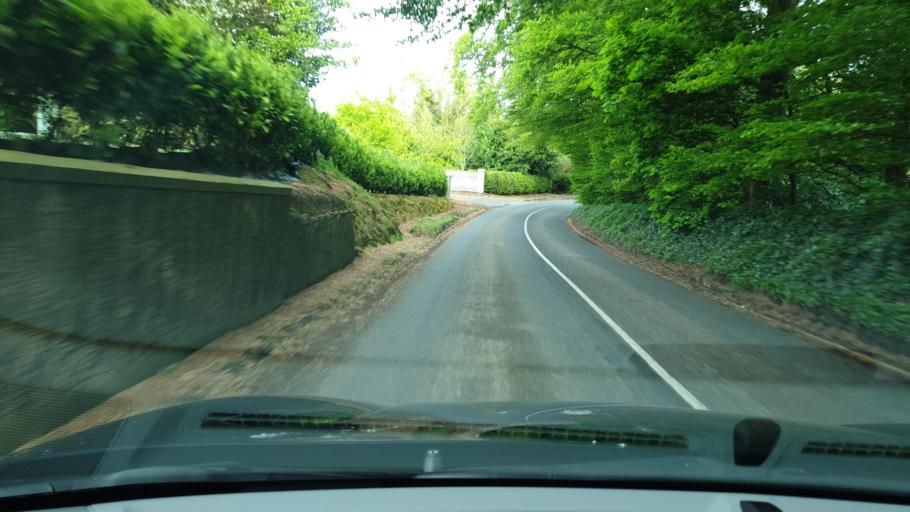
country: IE
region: Leinster
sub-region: An Mhi
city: Ashbourne
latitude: 53.5615
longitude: -6.3400
